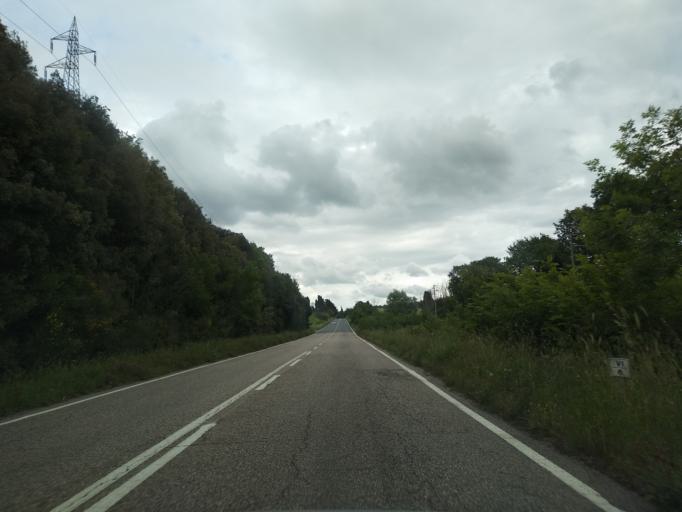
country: IT
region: Tuscany
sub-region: Provincia di Livorno
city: Guasticce
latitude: 43.5699
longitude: 10.4080
